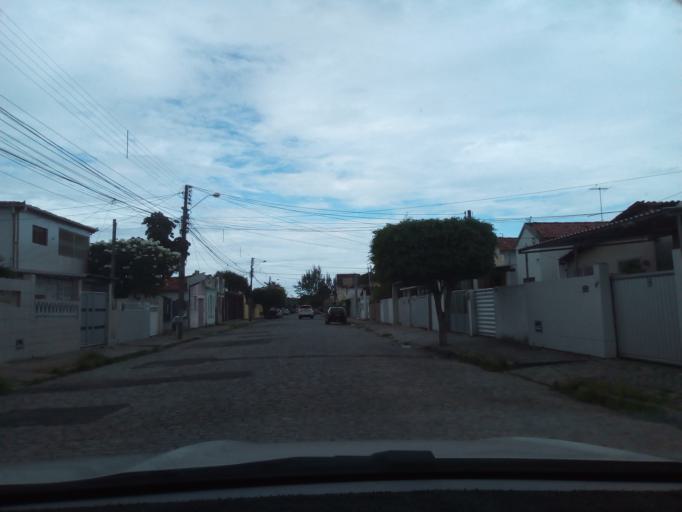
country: BR
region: Paraiba
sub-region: Joao Pessoa
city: Joao Pessoa
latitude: -7.1323
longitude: -34.8786
